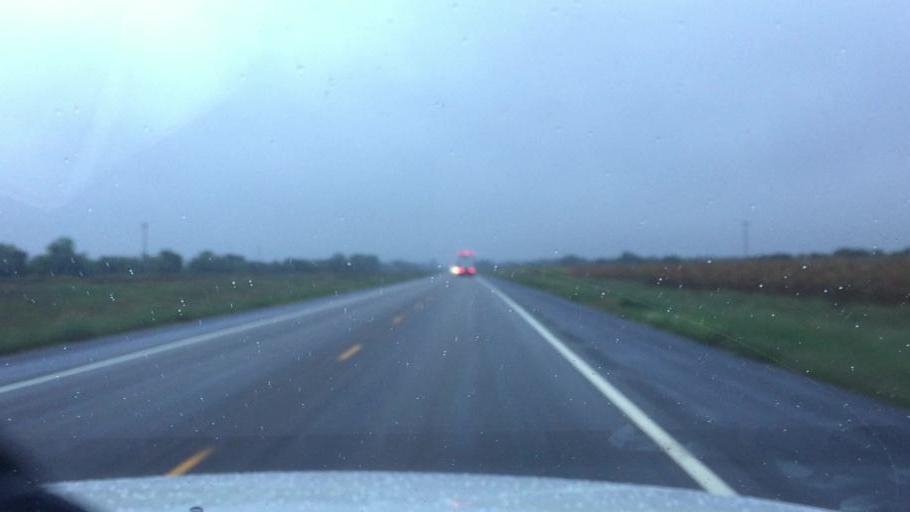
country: US
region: Kansas
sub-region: Montgomery County
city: Cherryvale
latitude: 37.4069
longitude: -95.5009
